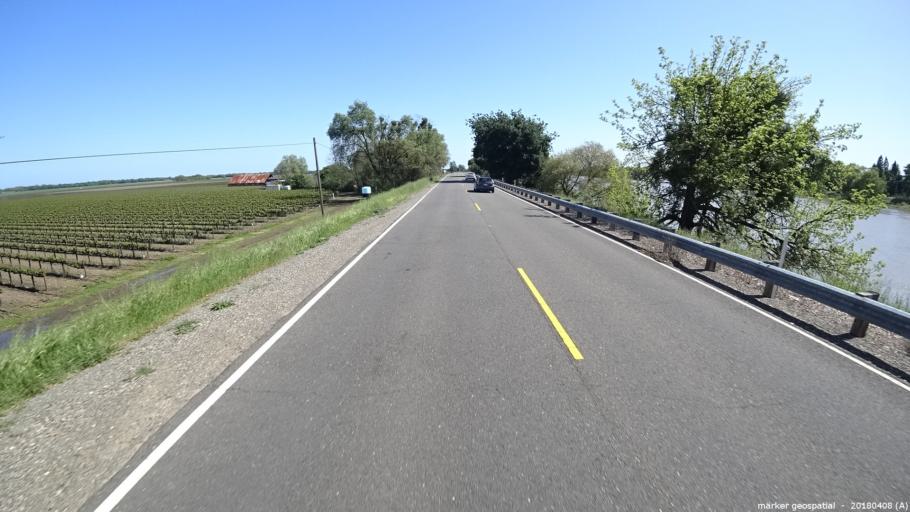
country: US
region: California
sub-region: Sacramento County
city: Parkway
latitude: 38.4222
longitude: -121.5257
